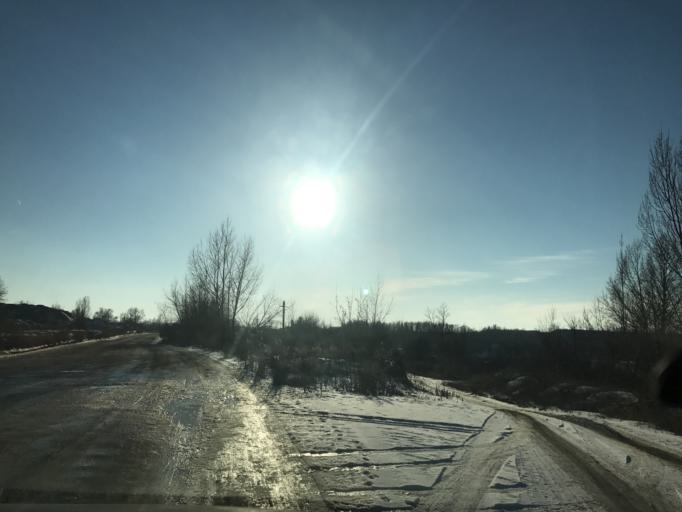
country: RU
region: Rostov
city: Staraya Stanitsa
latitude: 48.2364
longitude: 40.4013
